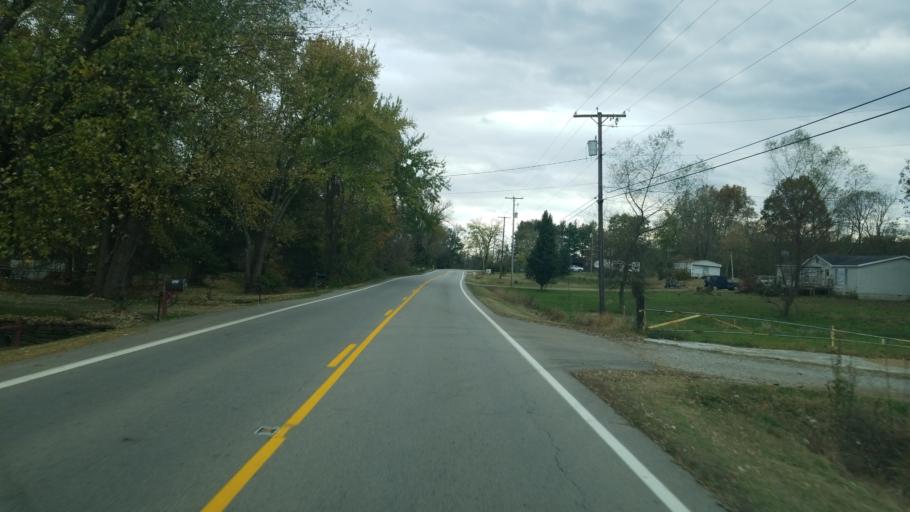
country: US
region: Ohio
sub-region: Scioto County
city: Lucasville
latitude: 38.9457
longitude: -83.0444
